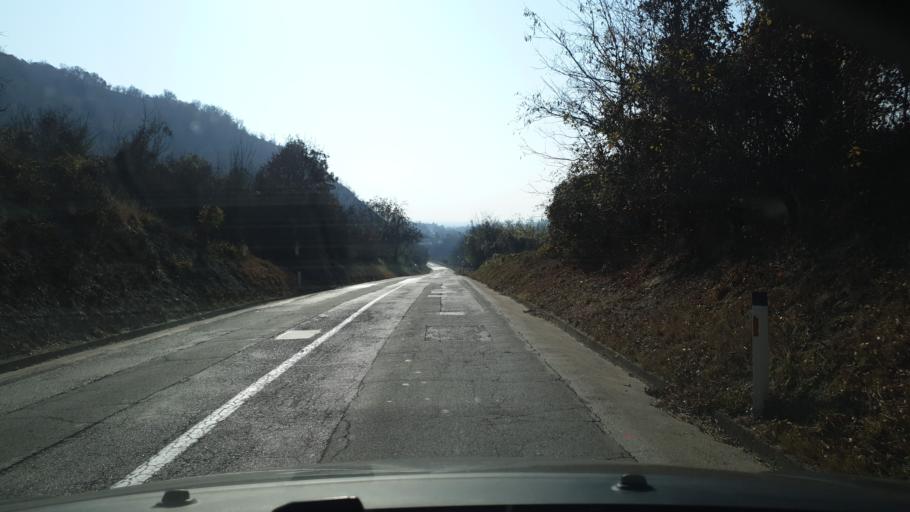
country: RS
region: Central Serbia
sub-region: Zajecarski Okrug
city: Zajecar
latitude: 43.7679
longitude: 22.3107
